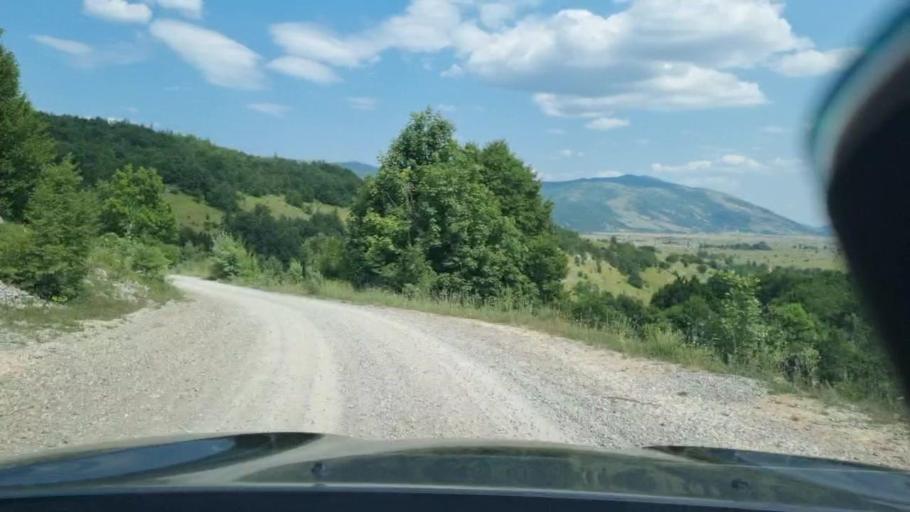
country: BA
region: Federation of Bosnia and Herzegovina
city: Bosansko Grahovo
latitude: 44.2981
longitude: 16.2726
